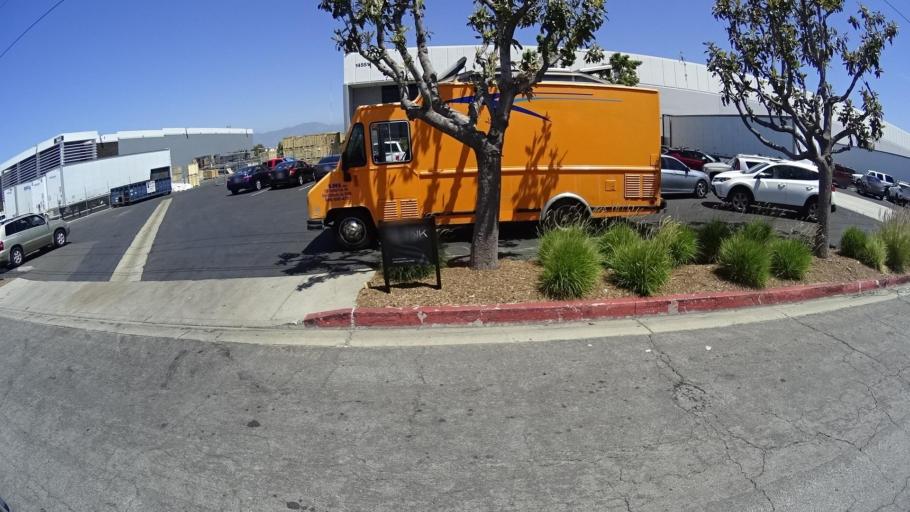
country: US
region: California
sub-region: Los Angeles County
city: Avocado Heights
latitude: 34.0260
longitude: -117.9860
